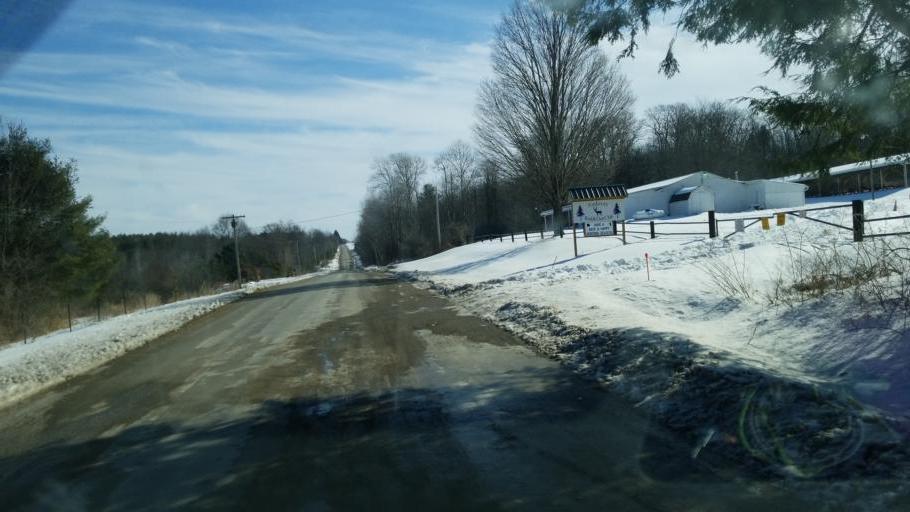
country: US
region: New York
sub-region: Allegany County
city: Andover
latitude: 42.1194
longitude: -77.7717
